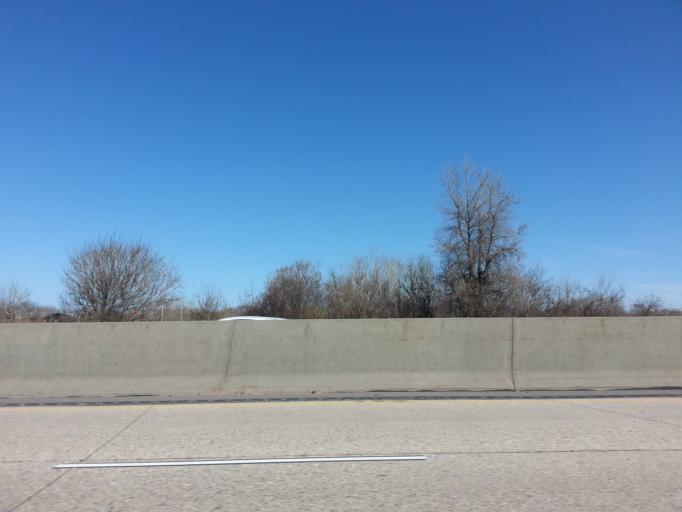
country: US
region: Minnesota
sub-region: Dakota County
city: Burnsville
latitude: 44.7295
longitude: -93.2830
